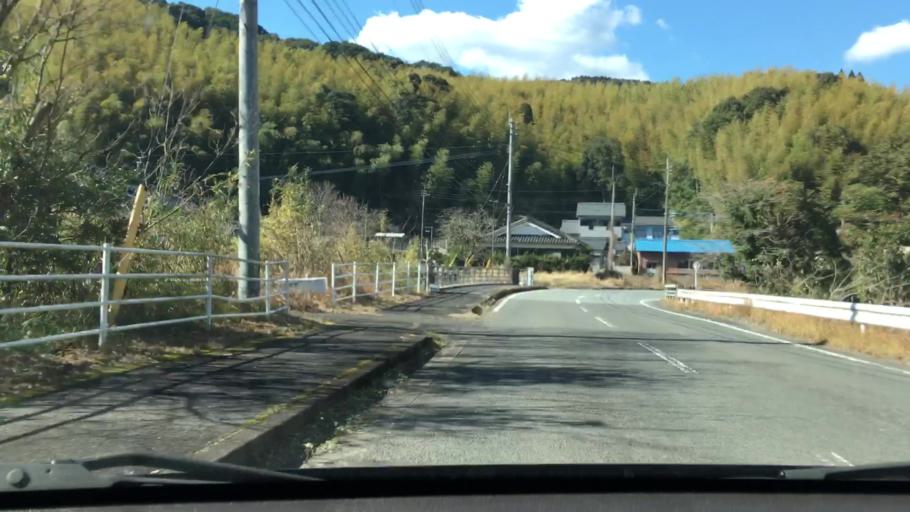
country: JP
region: Kagoshima
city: Ijuin
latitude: 31.7075
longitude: 130.4426
